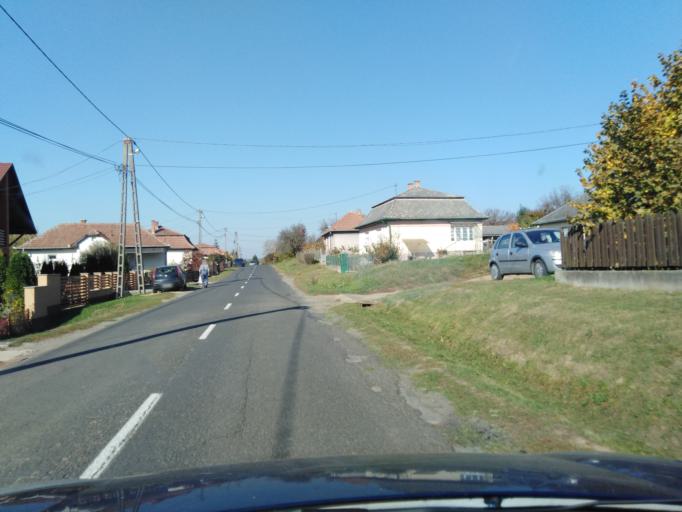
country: HU
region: Nograd
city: Karancskeszi
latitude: 48.1773
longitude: 19.6727
